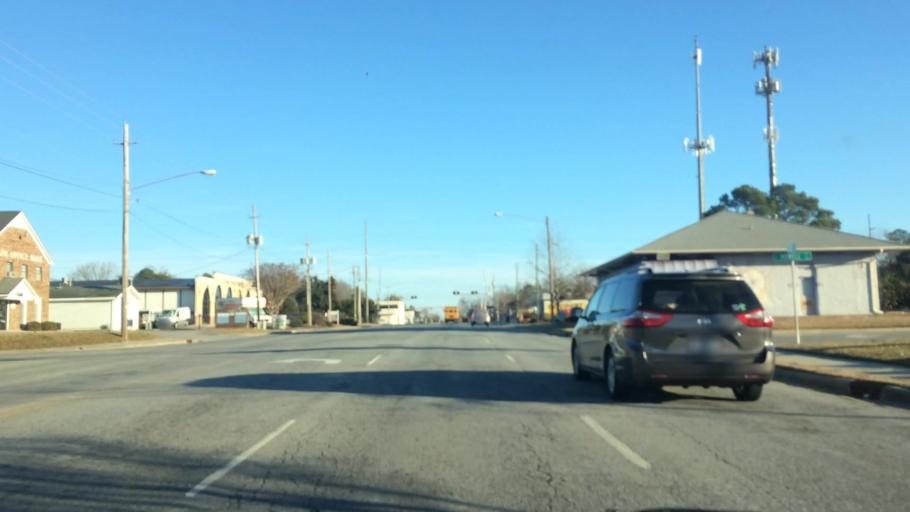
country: US
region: North Carolina
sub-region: Pitt County
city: Greenville
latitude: 35.5992
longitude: -77.3761
